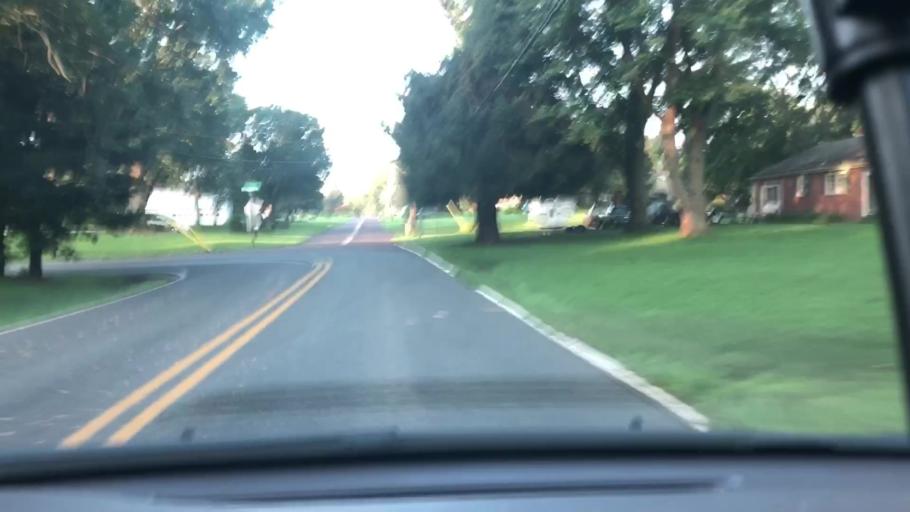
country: US
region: Pennsylvania
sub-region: Chester County
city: Kenilworth
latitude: 40.2121
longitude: -75.6254
